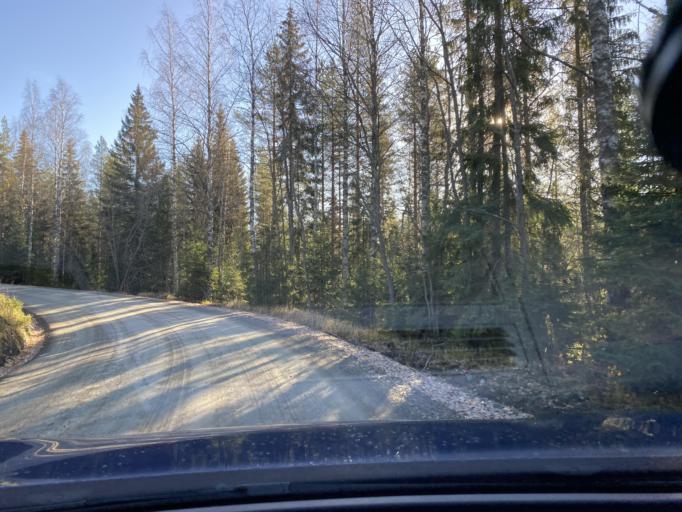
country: FI
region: Haeme
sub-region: Haemeenlinna
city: Kalvola
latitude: 60.9902
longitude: 24.0331
